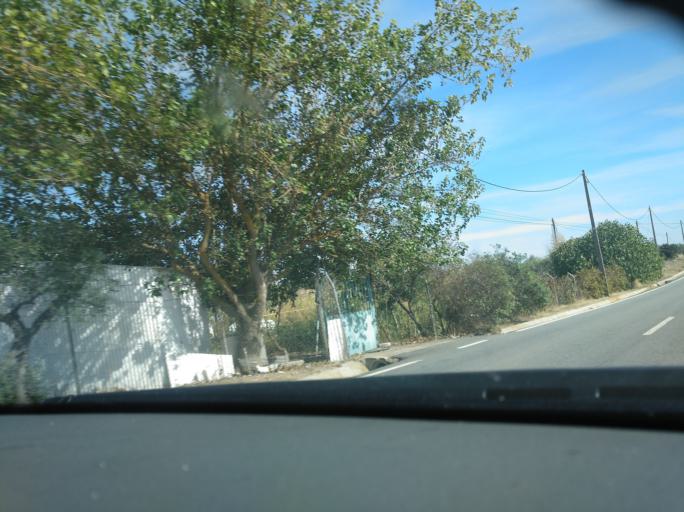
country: PT
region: Portalegre
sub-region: Campo Maior
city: Campo Maior
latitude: 38.9790
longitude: -7.0612
